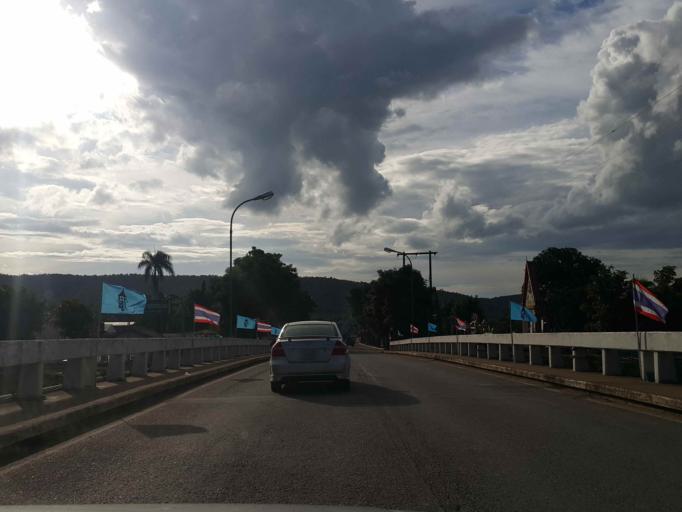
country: TH
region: Sukhothai
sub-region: Amphoe Si Satchanalai
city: Si Satchanalai
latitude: 17.5172
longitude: 99.7588
